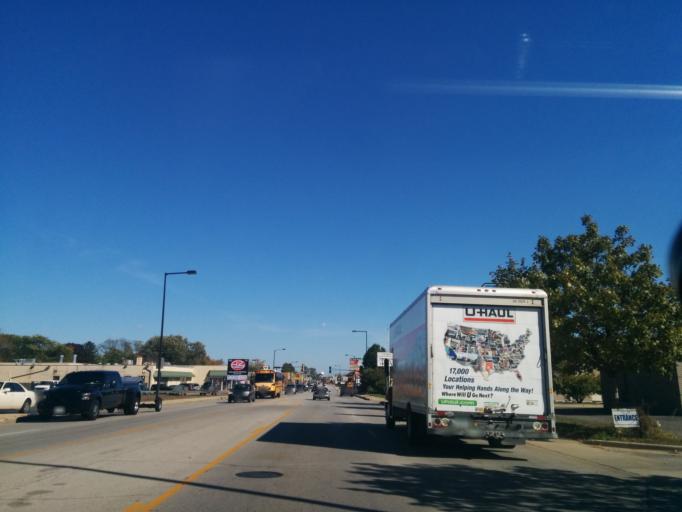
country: US
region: Illinois
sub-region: DuPage County
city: Villa Park
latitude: 41.8897
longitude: -87.9909
